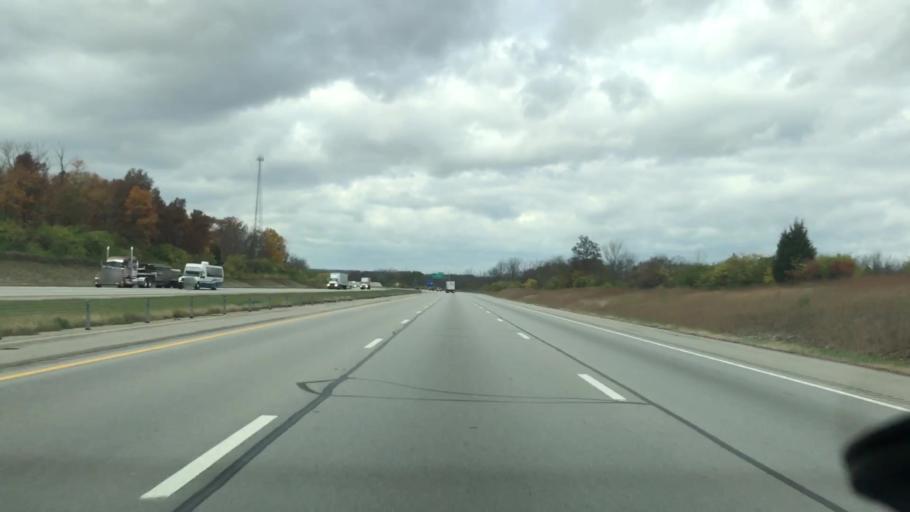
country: US
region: Ohio
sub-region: Clark County
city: Enon
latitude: 39.8936
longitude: -83.9093
